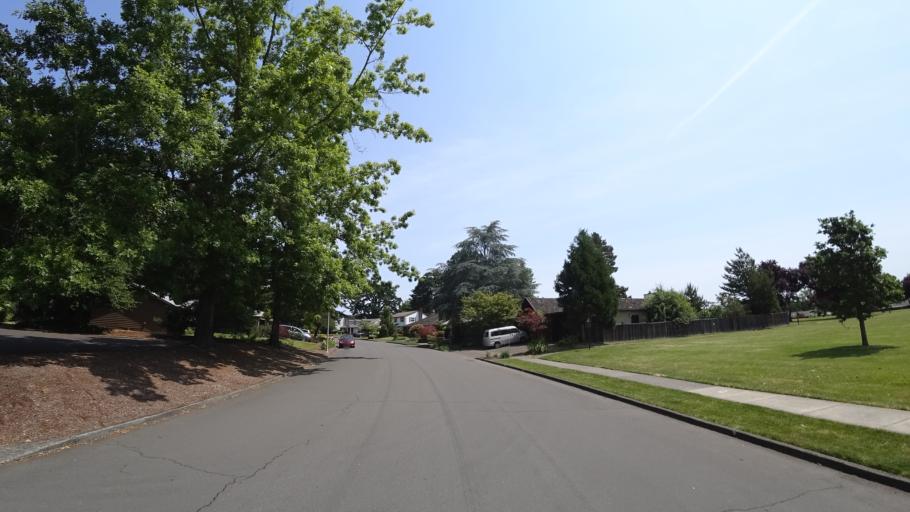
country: US
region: Oregon
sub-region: Washington County
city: Oak Hills
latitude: 45.5394
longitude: -122.8339
